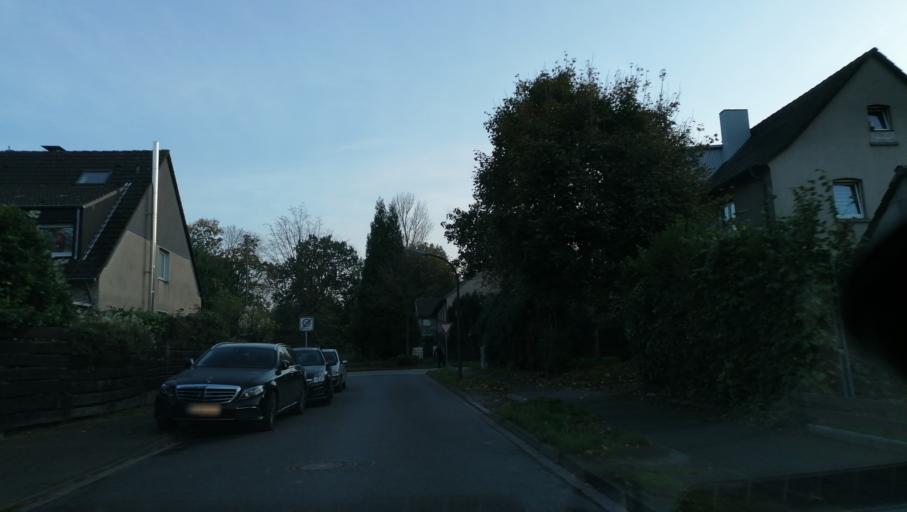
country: DE
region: North Rhine-Westphalia
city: Herten
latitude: 51.5734
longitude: 7.1758
